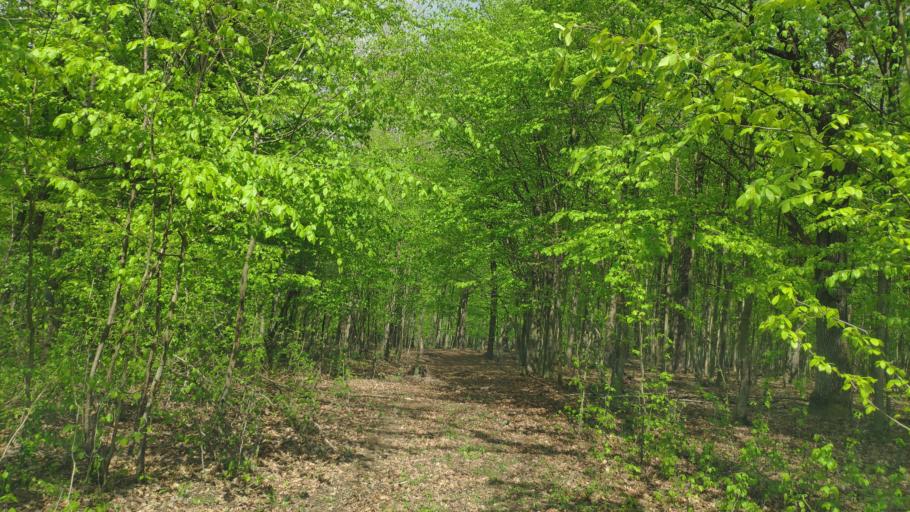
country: SK
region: Kosicky
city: Moldava nad Bodvou
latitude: 48.5486
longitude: 20.9349
